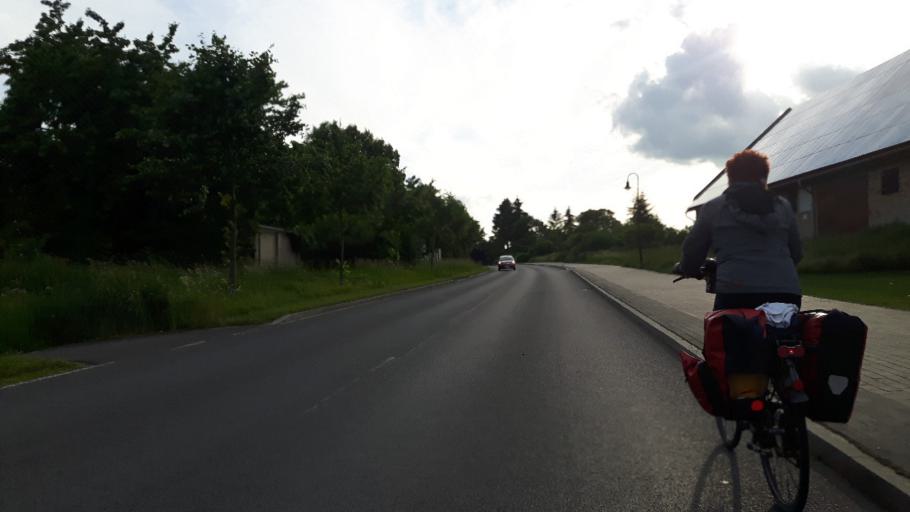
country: DE
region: Brandenburg
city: Gartz
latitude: 53.2109
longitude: 14.3912
